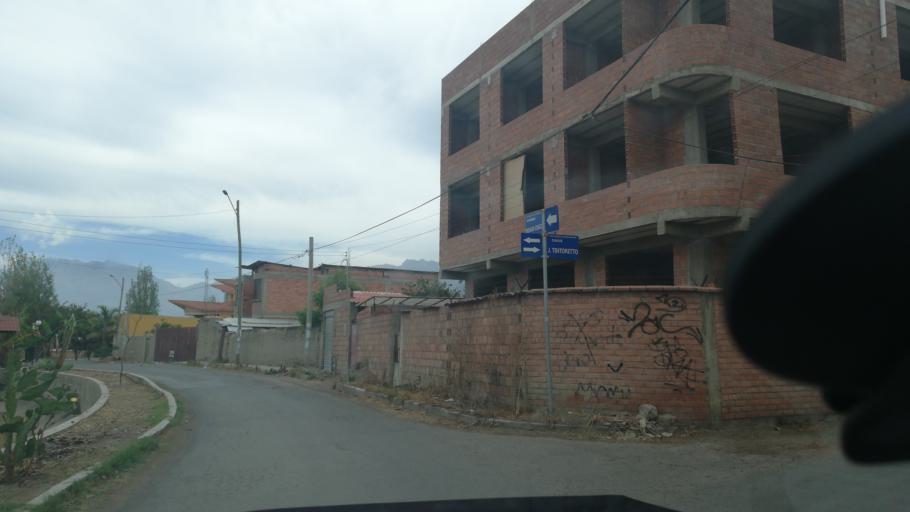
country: BO
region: Cochabamba
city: Cochabamba
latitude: -17.3618
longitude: -66.1872
